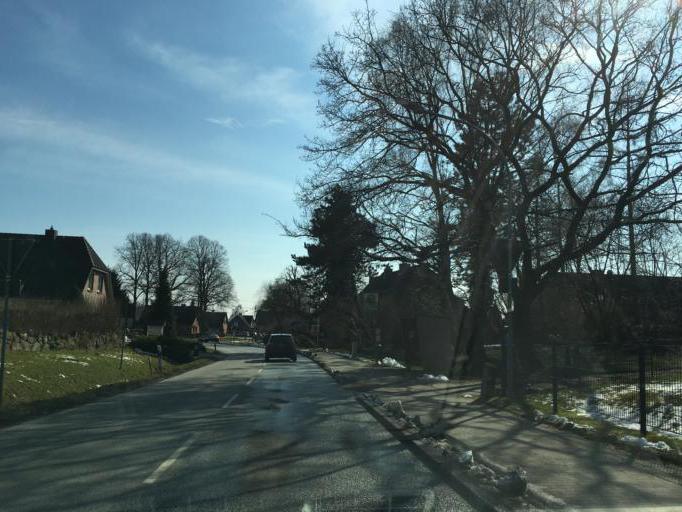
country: DE
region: Schleswig-Holstein
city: Kroppelshagen-Fahrendorf
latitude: 53.4879
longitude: 10.3156
